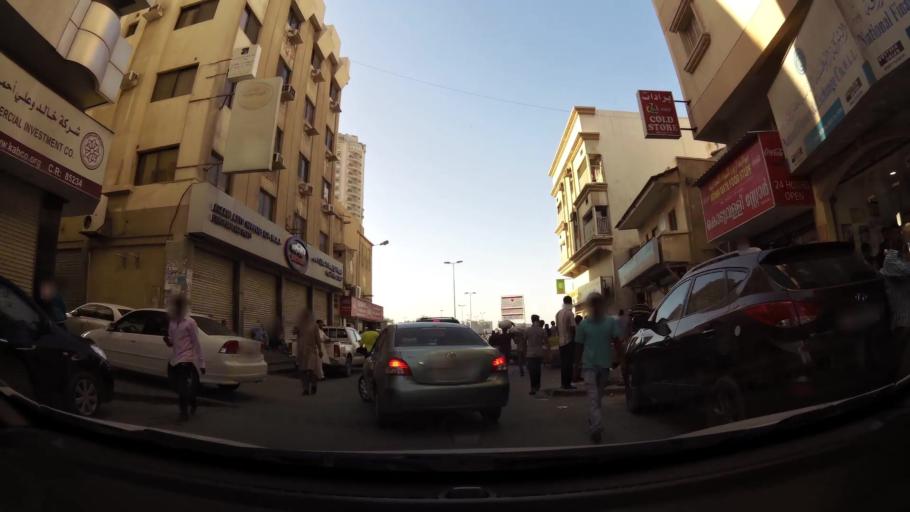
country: BH
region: Manama
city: Manama
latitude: 26.2297
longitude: 50.5713
